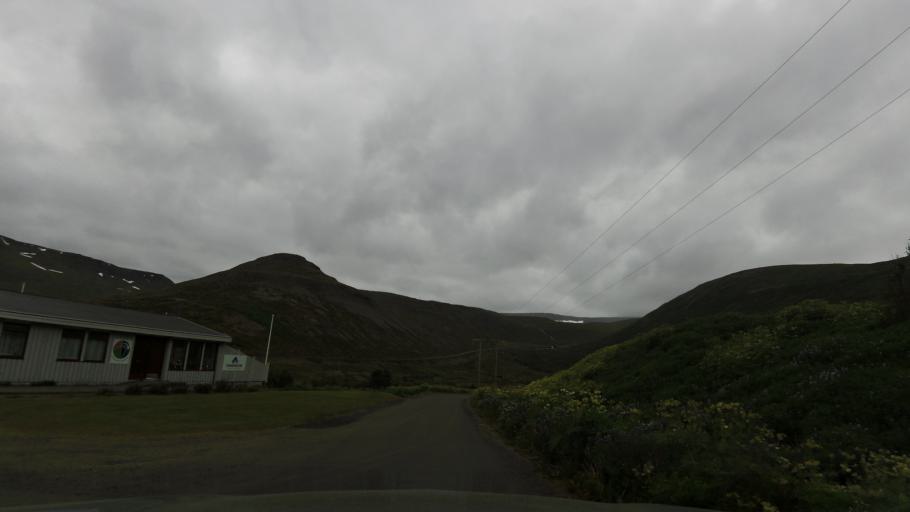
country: IS
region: Westfjords
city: Isafjoerdur
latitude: 66.0610
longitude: -23.1924
